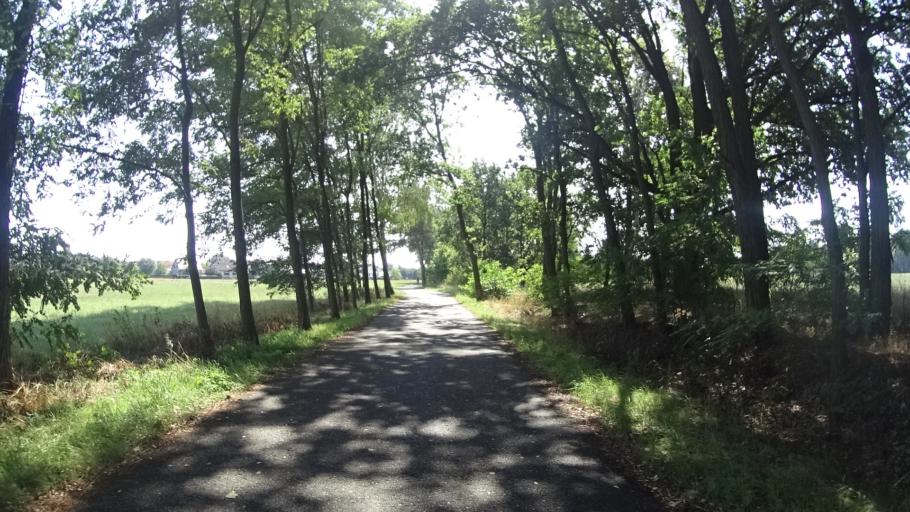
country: DE
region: Brandenburg
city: Cottbus
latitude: 51.7946
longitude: 14.2996
